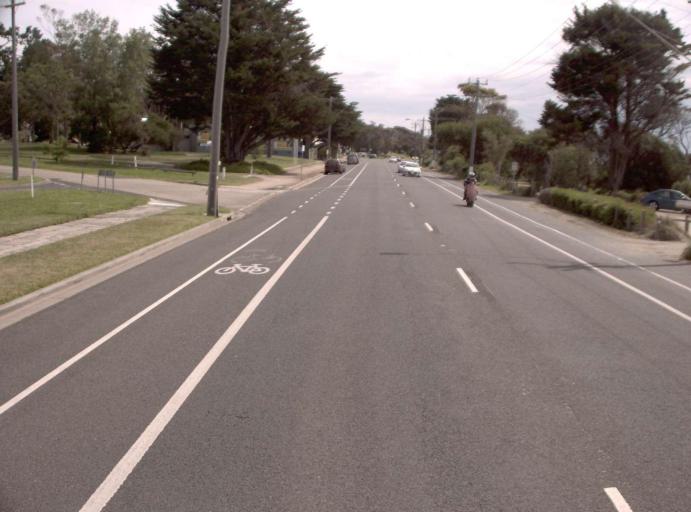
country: AU
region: Victoria
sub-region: Mornington Peninsula
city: Dromana
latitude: -38.3362
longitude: 144.9576
